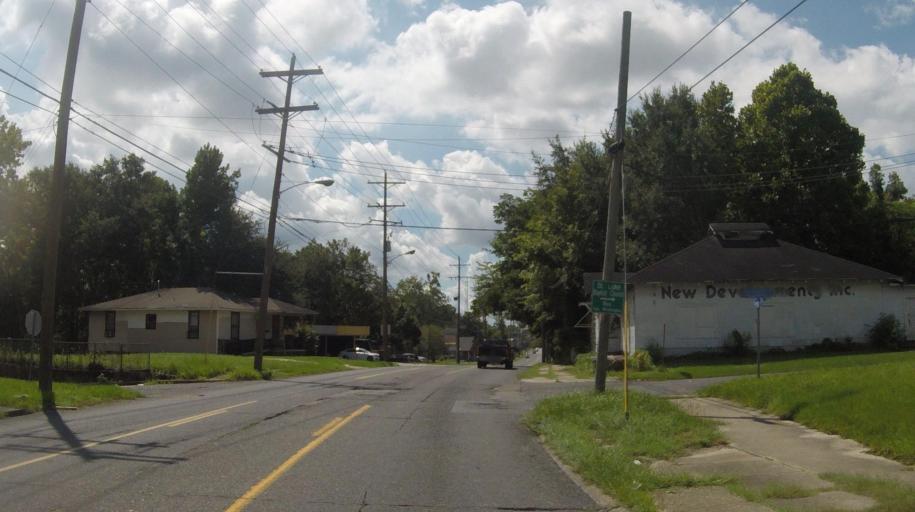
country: US
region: Louisiana
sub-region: East Baton Rouge Parish
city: Baton Rouge
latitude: 30.4304
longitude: -91.1822
